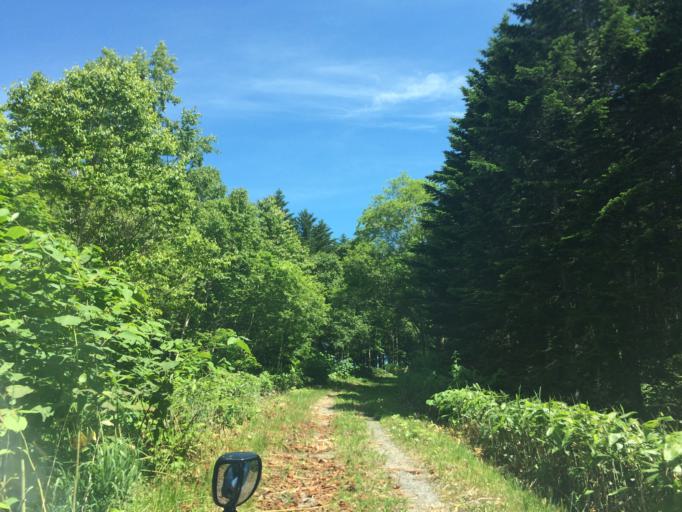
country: JP
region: Hokkaido
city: Niseko Town
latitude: 42.8625
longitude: 140.8165
